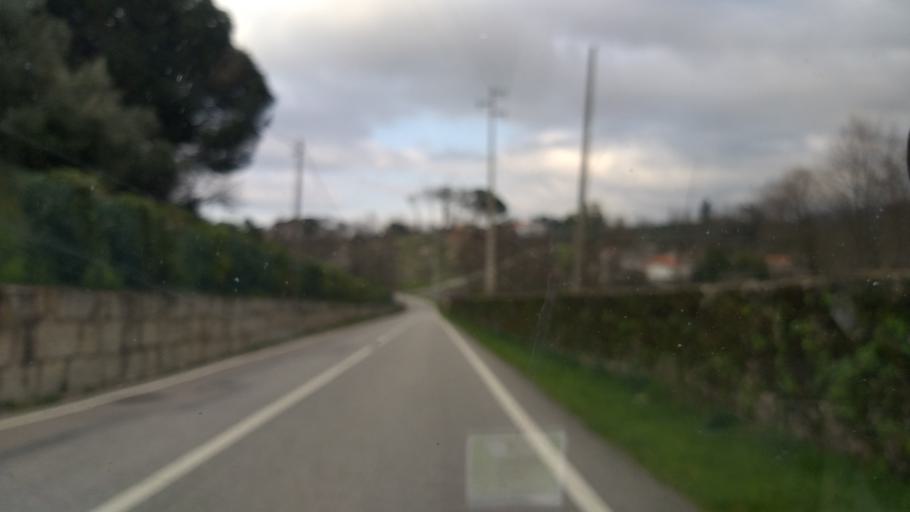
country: PT
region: Guarda
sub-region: Seia
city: Seia
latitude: 40.4837
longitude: -7.6342
